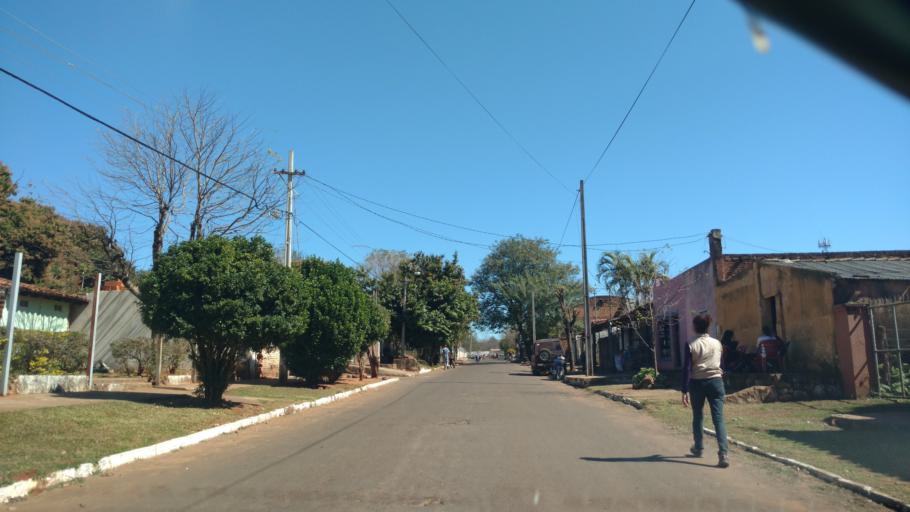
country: PY
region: Paraguari
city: Yaguaron
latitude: -25.5624
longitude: -57.2882
